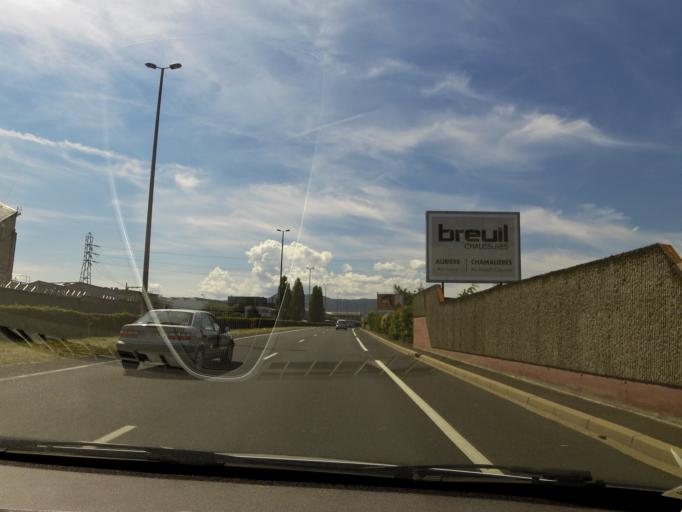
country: FR
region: Auvergne
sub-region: Departement du Puy-de-Dome
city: Clermont-Ferrand
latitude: 45.7976
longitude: 3.1083
